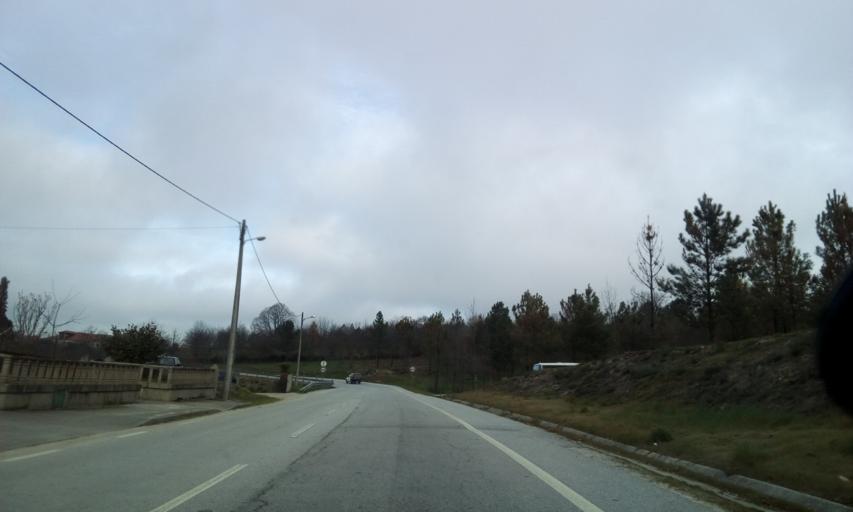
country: PT
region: Guarda
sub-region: Aguiar da Beira
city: Aguiar da Beira
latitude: 40.7252
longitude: -7.4938
